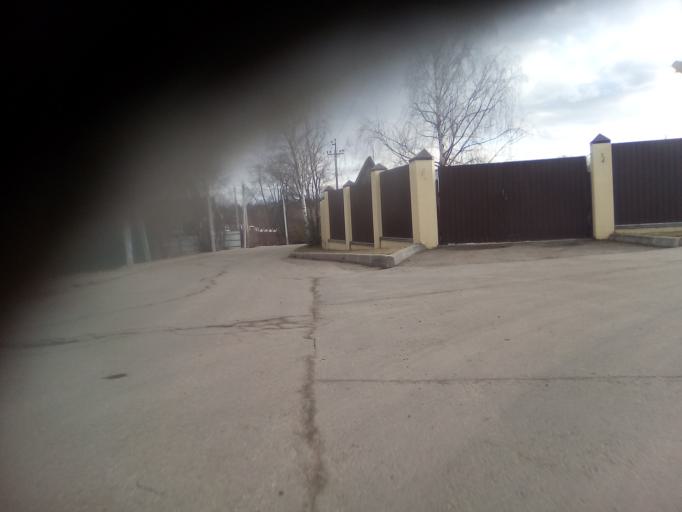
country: RU
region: Moskovskaya
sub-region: Leninskiy Rayon
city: Vnukovo
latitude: 55.5911
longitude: 37.3209
